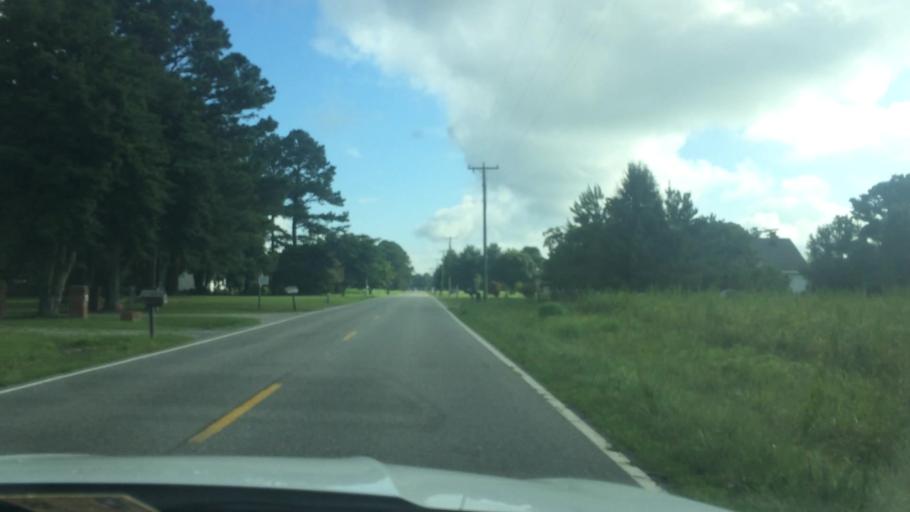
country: US
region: Virginia
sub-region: Gloucester County
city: Gloucester Courthouse
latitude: 37.4860
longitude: -76.4414
